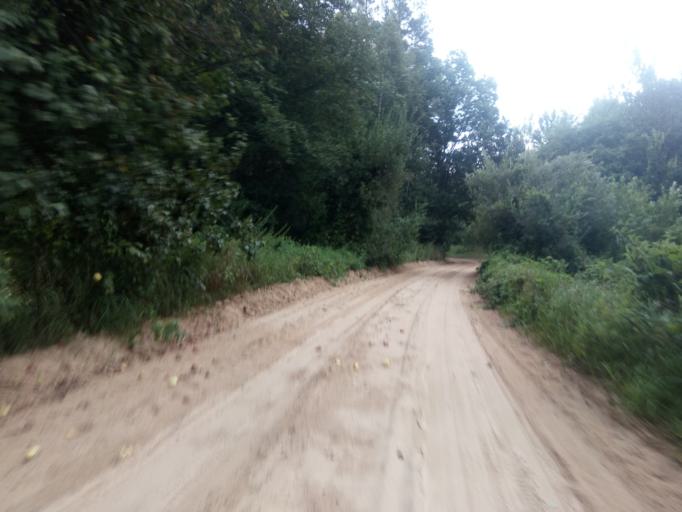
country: BY
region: Vitebsk
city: Dzisna
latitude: 55.7055
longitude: 28.3333
